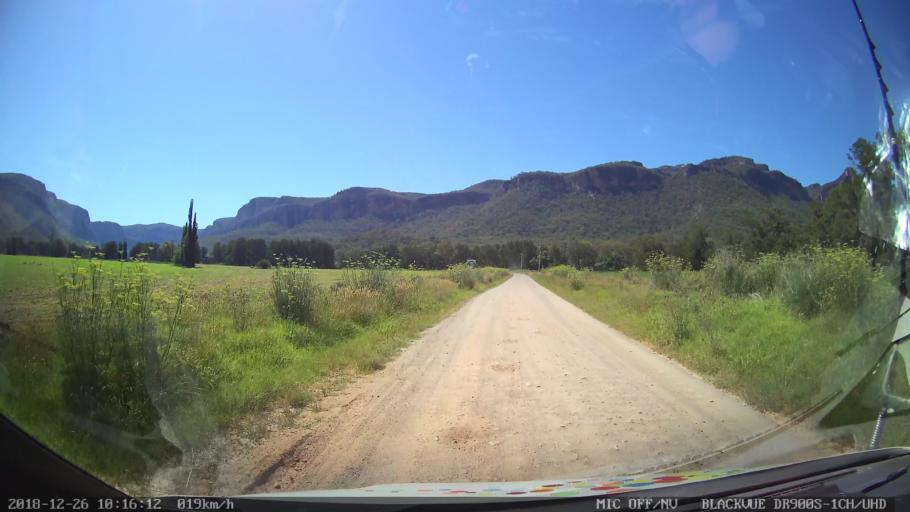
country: AU
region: New South Wales
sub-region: Lithgow
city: Portland
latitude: -33.1201
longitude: 150.2768
